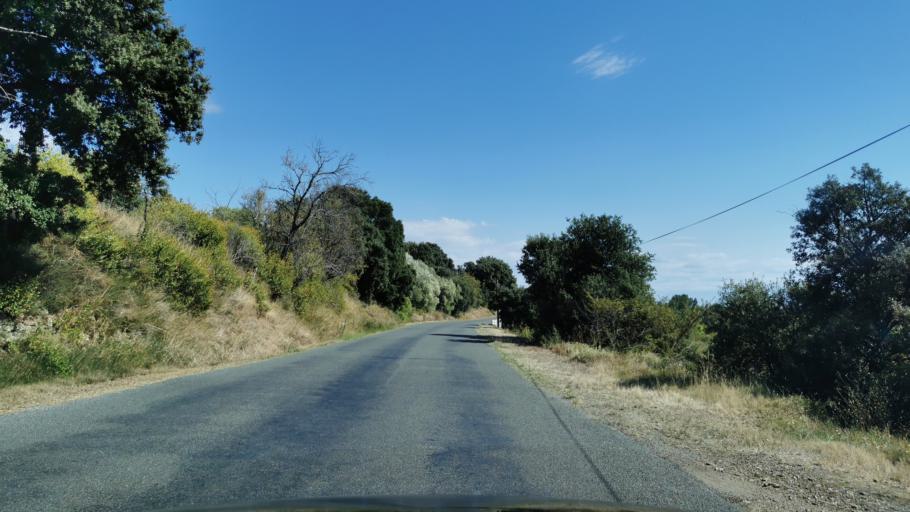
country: FR
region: Languedoc-Roussillon
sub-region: Departement de l'Aude
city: Caunes-Minervois
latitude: 43.3157
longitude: 2.5482
